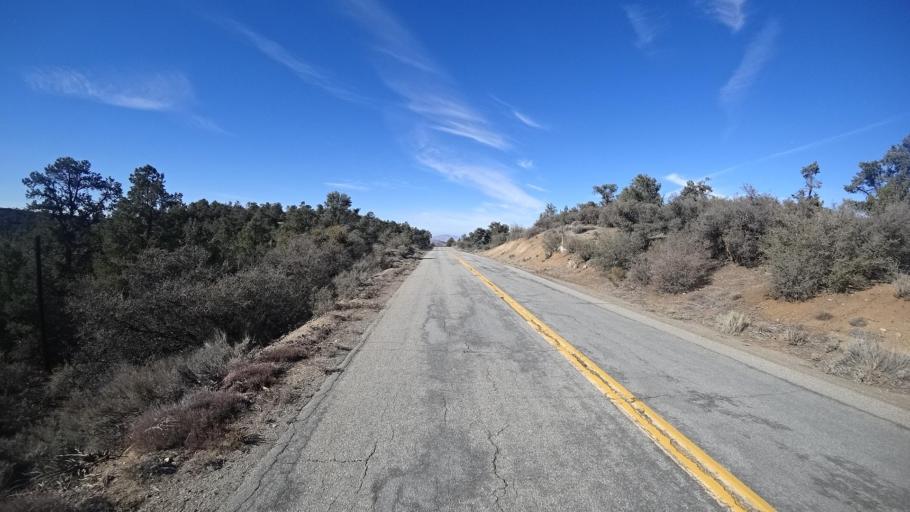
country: US
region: California
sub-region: Kern County
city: Pine Mountain Club
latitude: 34.8706
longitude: -119.2652
